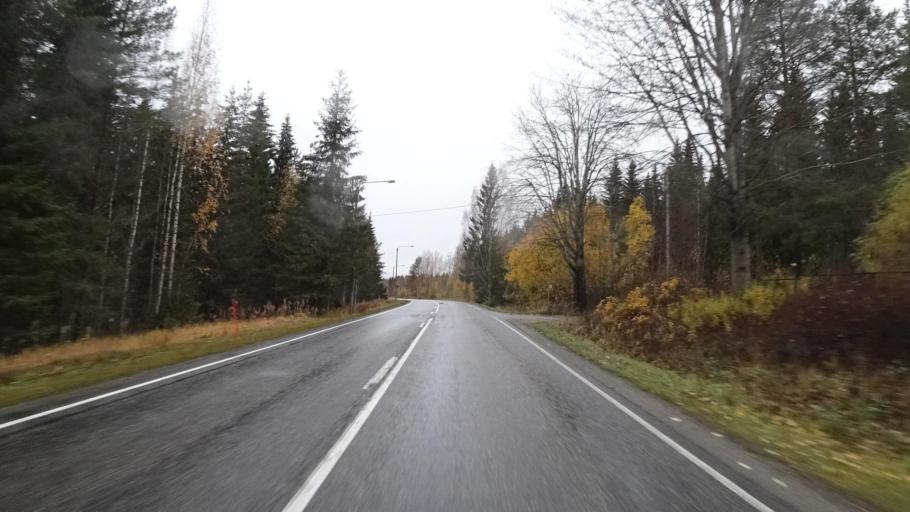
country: FI
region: Northern Savo
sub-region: Koillis-Savo
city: Tuusniemi
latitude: 62.7923
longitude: 28.5590
